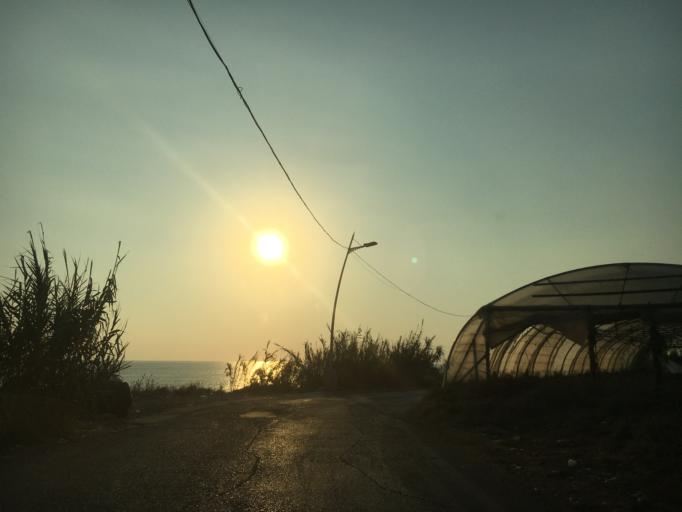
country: LB
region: Mont-Liban
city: Jbail
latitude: 34.1375
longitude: 35.6371
